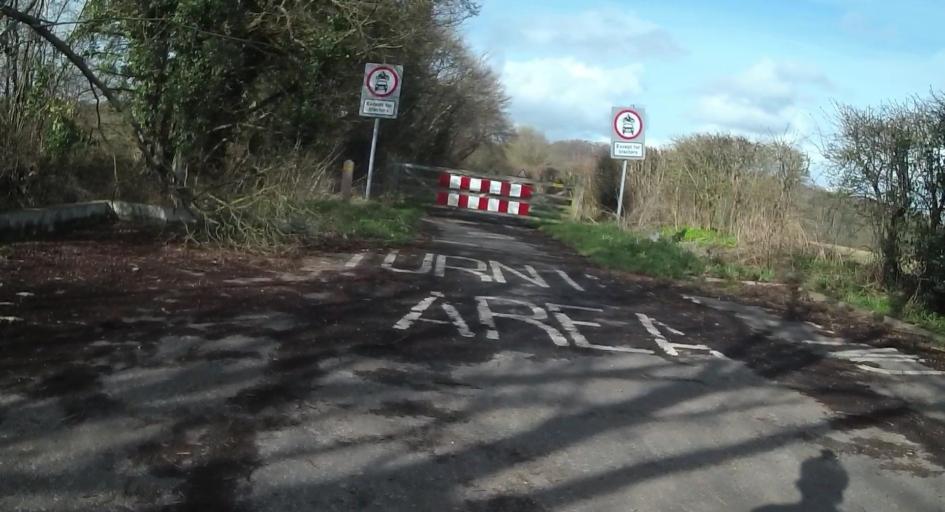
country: GB
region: England
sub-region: West Berkshire
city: Thatcham
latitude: 51.3694
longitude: -1.2534
